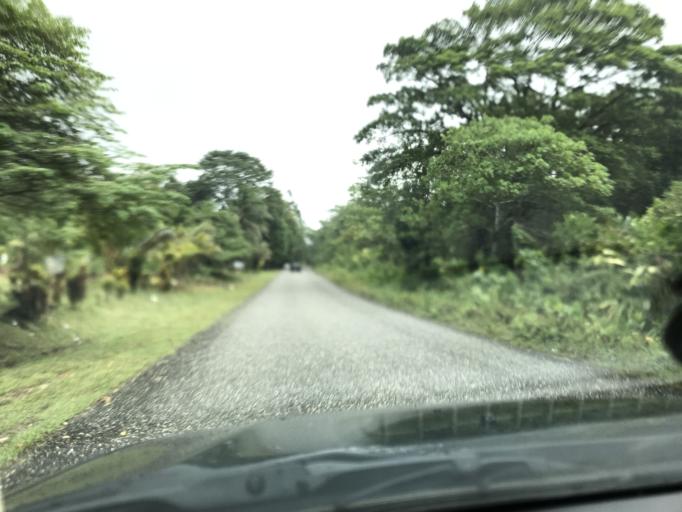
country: SB
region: Western Province
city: Gizo
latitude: -8.2420
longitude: 157.2331
